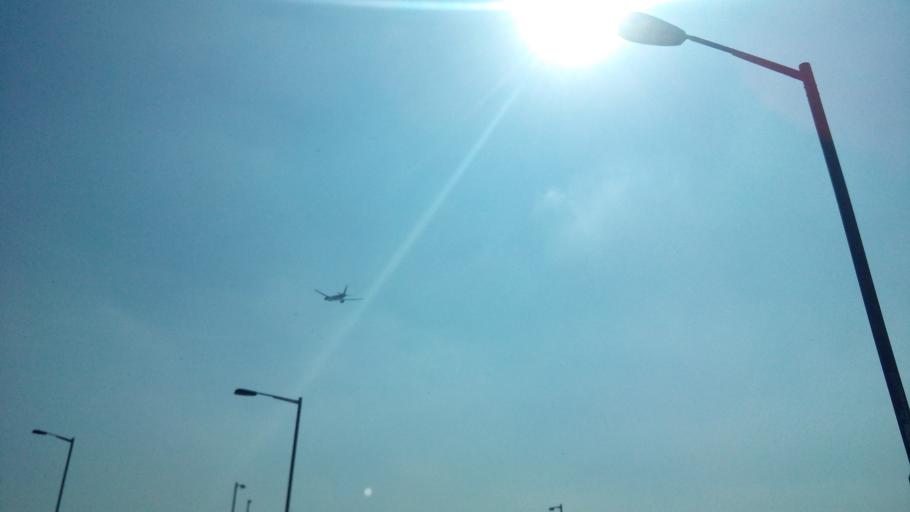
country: HK
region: Tuen Mun
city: Tuen Mun
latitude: 22.3109
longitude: 113.9370
